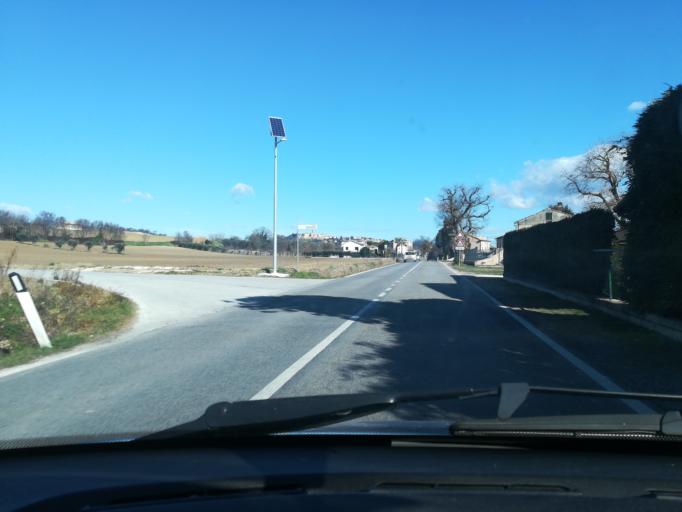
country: IT
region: The Marches
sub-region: Provincia di Macerata
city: Villa Potenza
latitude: 43.3403
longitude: 13.4305
